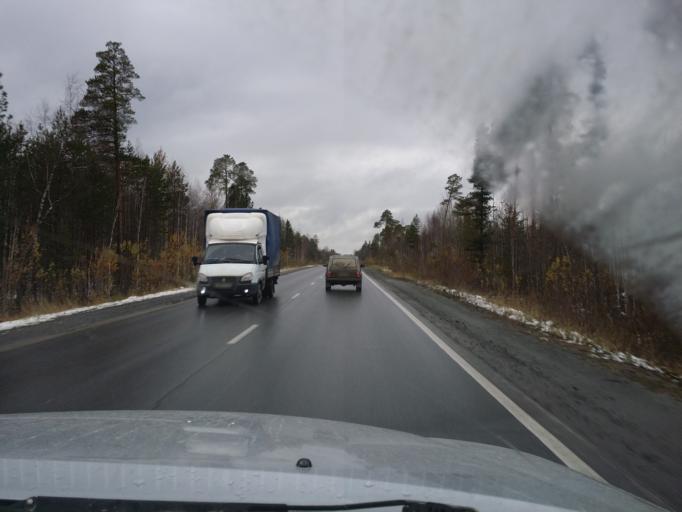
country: RU
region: Khanty-Mansiyskiy Avtonomnyy Okrug
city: Megion
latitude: 61.1269
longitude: 75.8098
